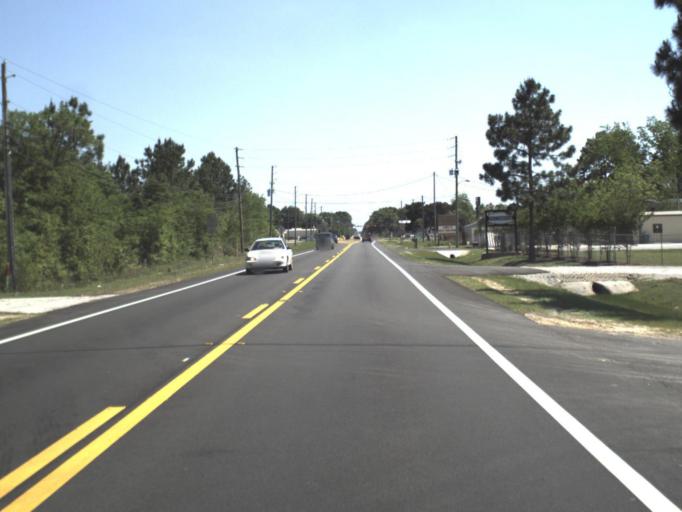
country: US
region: Florida
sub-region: Bay County
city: Cedar Grove
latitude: 30.1787
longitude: -85.6078
